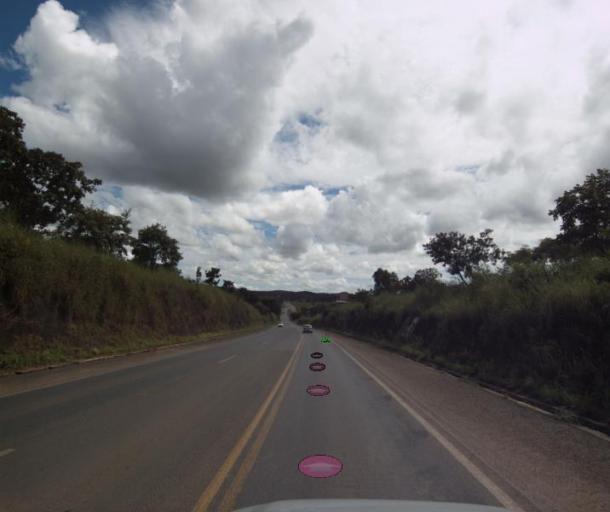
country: BR
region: Goias
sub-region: Uruacu
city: Uruacu
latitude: -14.5074
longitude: -49.1483
